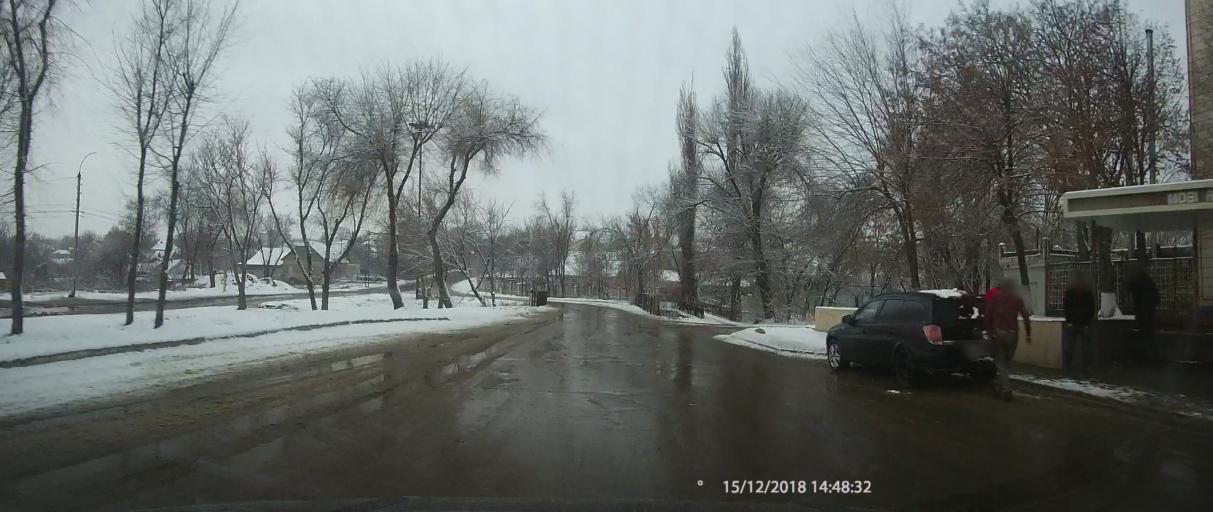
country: MD
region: Cahul
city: Cahul
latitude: 45.8981
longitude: 28.1976
